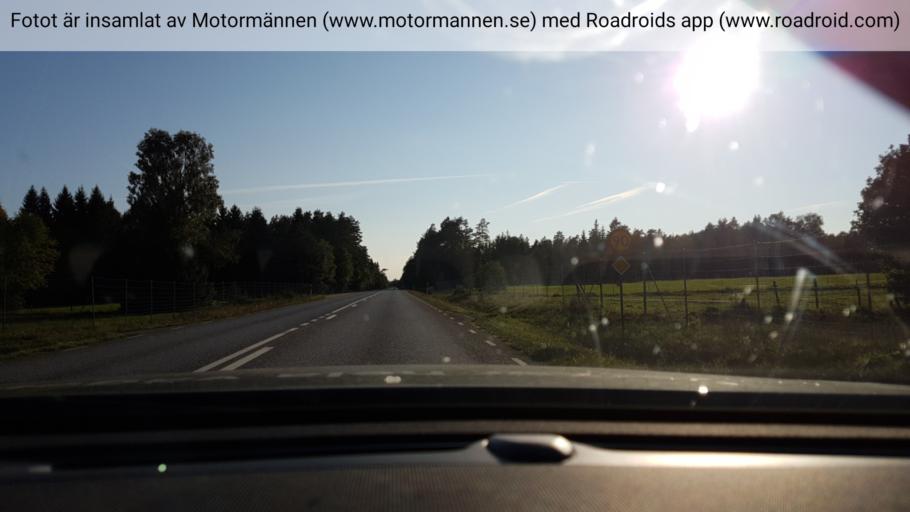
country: SE
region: Halland
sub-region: Hylte Kommun
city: Hyltebruk
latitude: 57.0545
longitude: 13.3325
